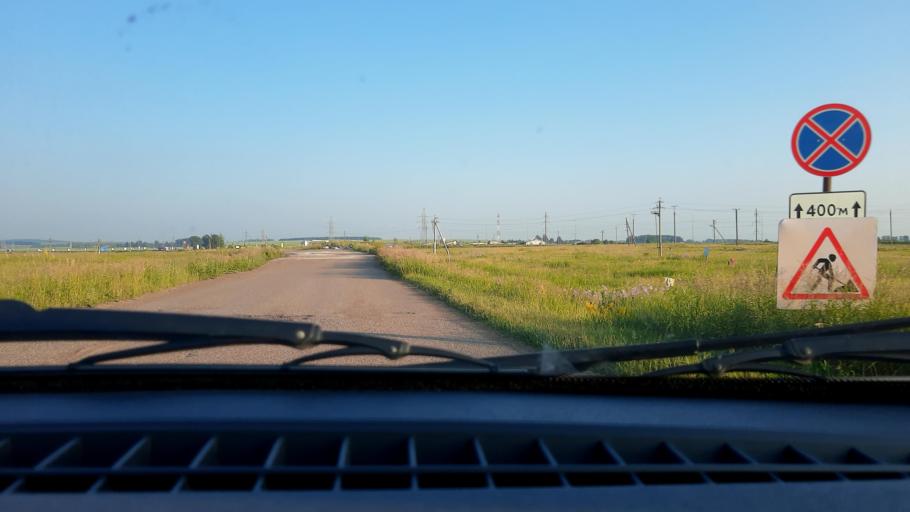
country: RU
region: Bashkortostan
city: Asanovo
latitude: 54.9055
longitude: 55.6276
